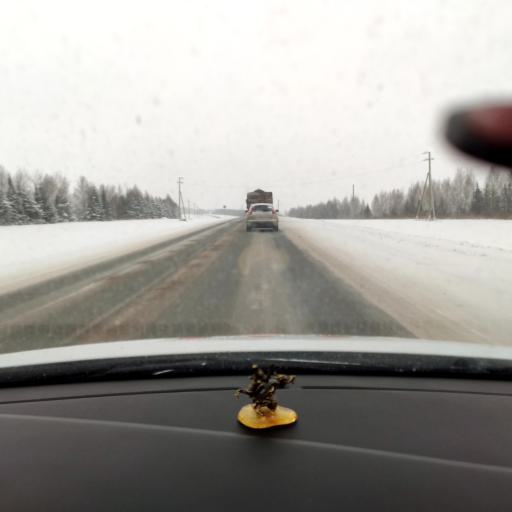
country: RU
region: Tatarstan
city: Vysokaya Gora
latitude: 56.0243
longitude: 49.2566
